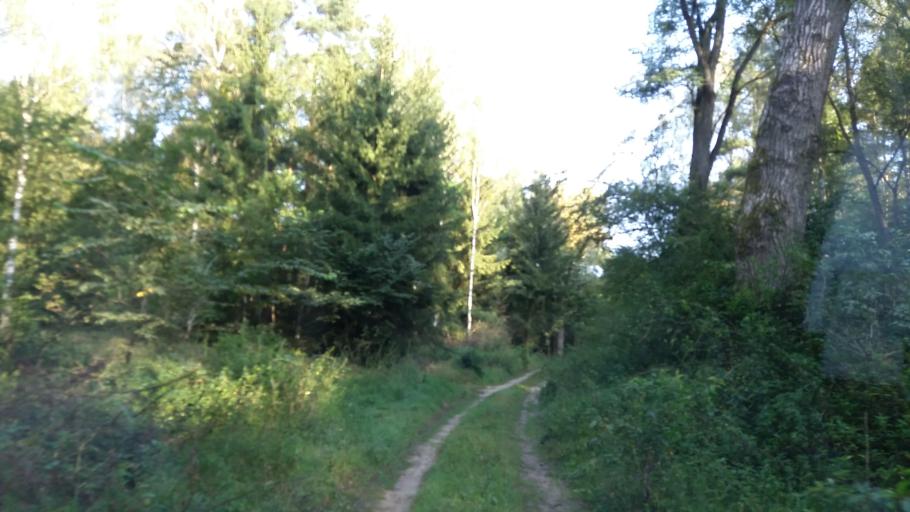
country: PL
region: West Pomeranian Voivodeship
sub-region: Powiat choszczenski
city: Recz
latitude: 53.1944
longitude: 15.5417
